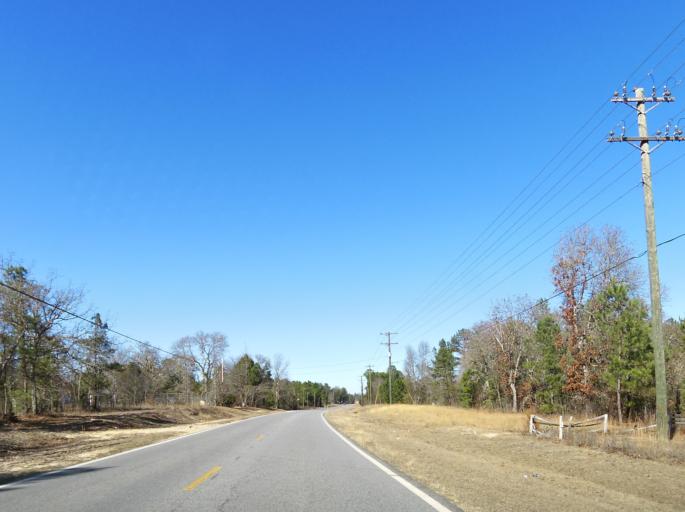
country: US
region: Georgia
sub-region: Bibb County
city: West Point
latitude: 32.7865
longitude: -83.7910
